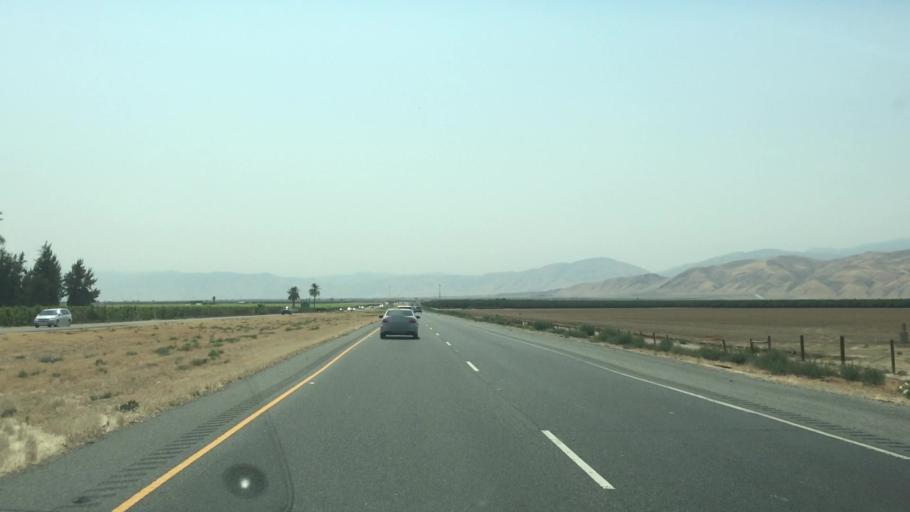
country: US
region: California
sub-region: Kern County
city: Greenfield
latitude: 35.0918
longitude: -119.0341
